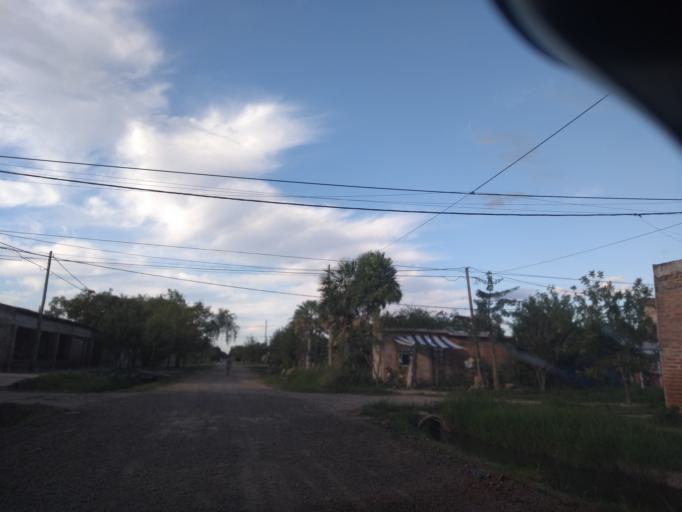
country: AR
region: Chaco
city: Barranqueras
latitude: -27.4921
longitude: -58.9393
